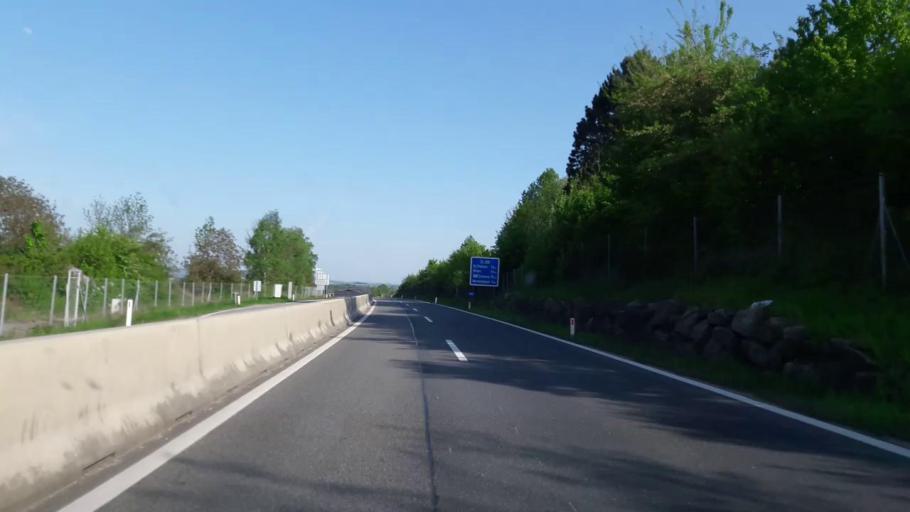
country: AT
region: Lower Austria
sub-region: Politischer Bezirk Hollabrunn
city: Gollersdorf
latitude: 48.4890
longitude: 16.1129
